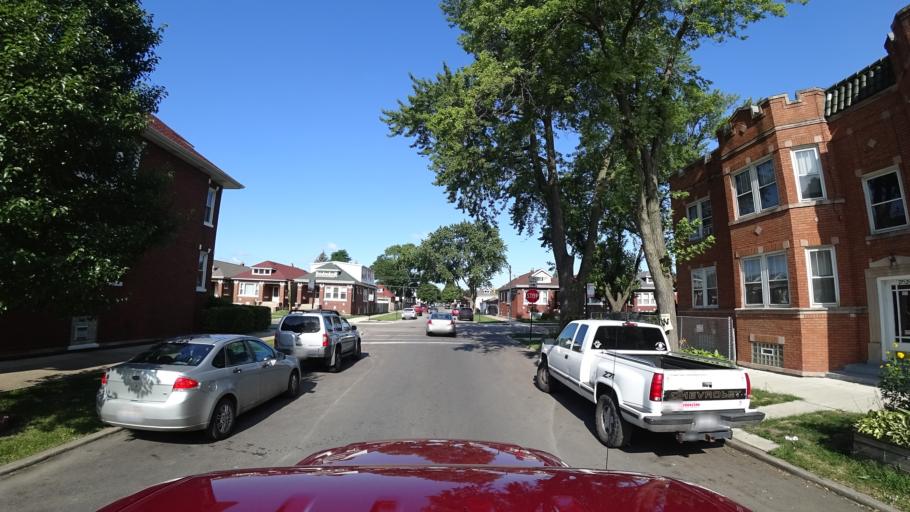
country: US
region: Illinois
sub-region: Cook County
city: Hometown
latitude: 41.7900
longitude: -87.6982
